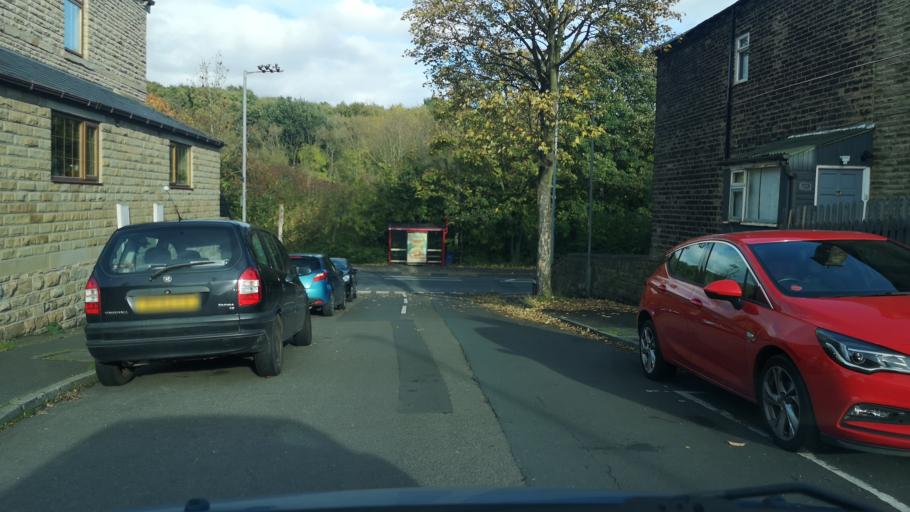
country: GB
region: England
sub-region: Kirklees
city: Batley
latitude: 53.7230
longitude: -1.6480
